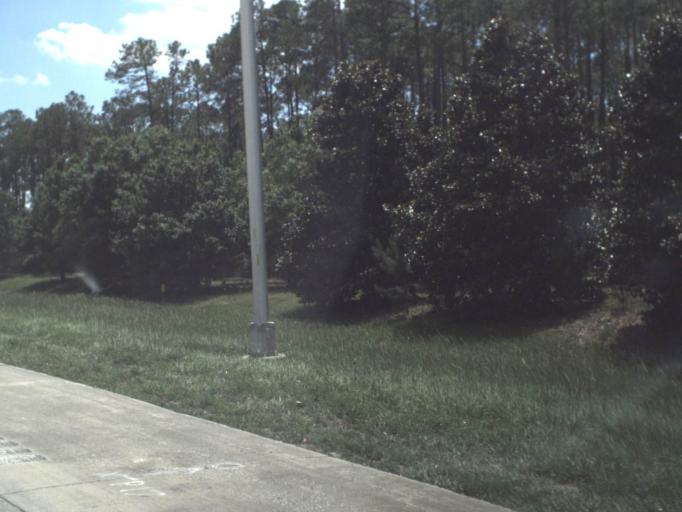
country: US
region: Florida
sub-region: Saint Johns County
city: Palm Valley
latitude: 30.1841
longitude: -81.5140
